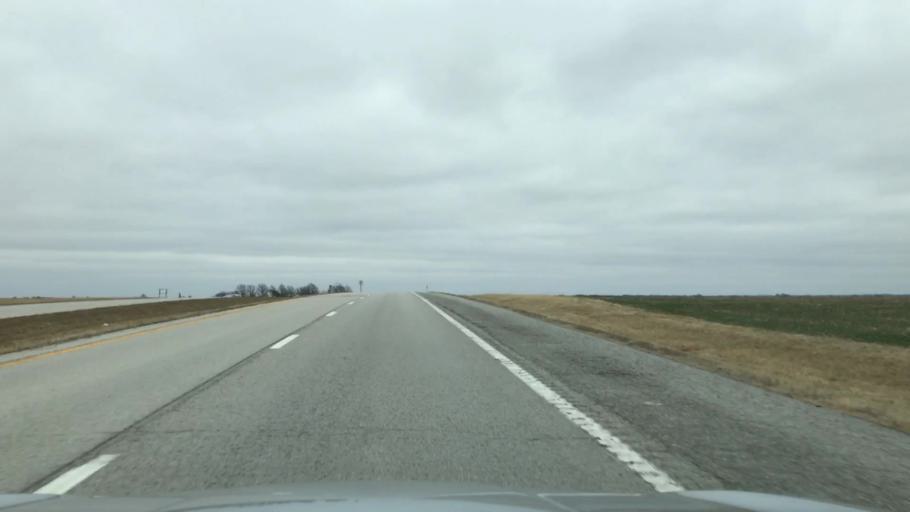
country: US
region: Missouri
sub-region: Livingston County
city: Chillicothe
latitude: 39.7762
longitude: -93.4797
